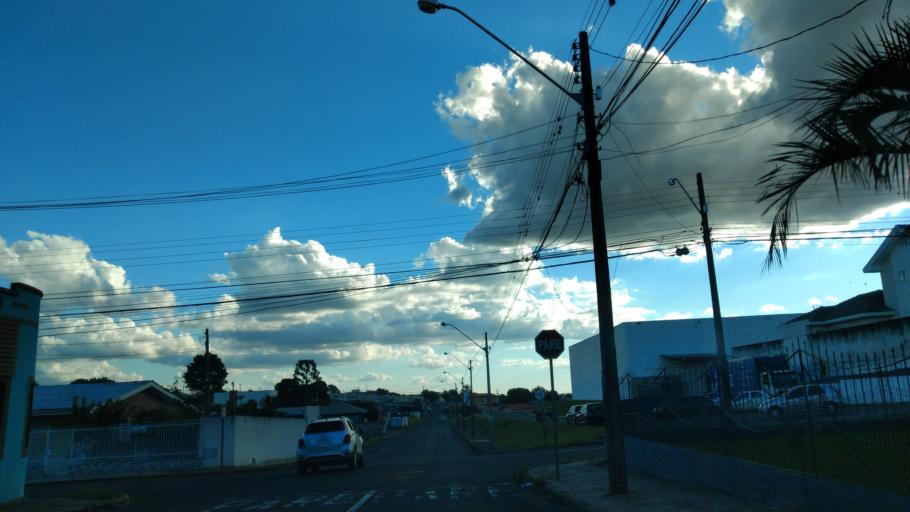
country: BR
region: Parana
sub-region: Guarapuava
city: Guarapuava
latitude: -25.3929
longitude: -51.4786
